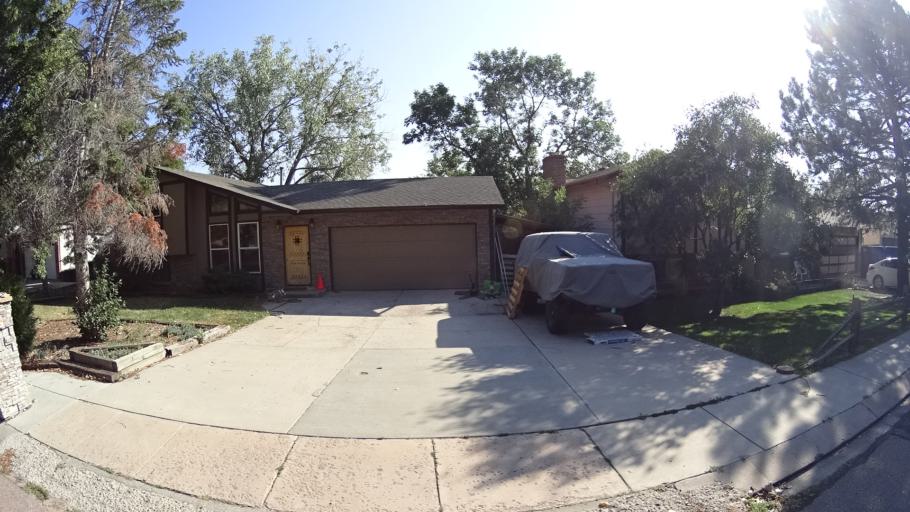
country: US
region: Colorado
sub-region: El Paso County
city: Colorado Springs
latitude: 38.8858
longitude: -104.8423
